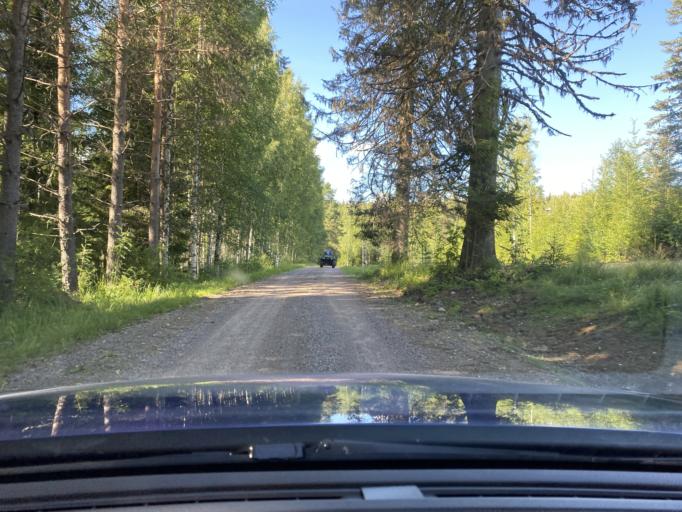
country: FI
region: Pirkanmaa
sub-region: Ylae-Pirkanmaa
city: Maenttae
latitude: 62.0169
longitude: 24.7418
